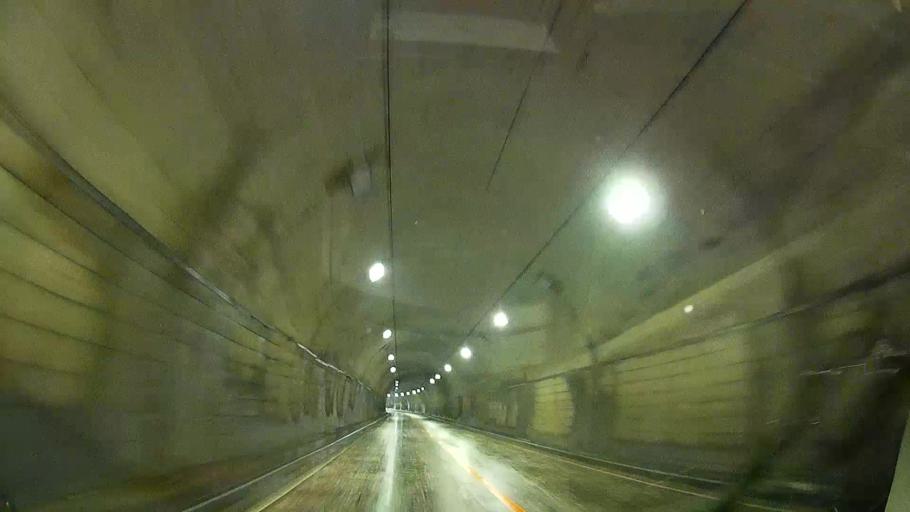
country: JP
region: Kumamoto
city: Aso
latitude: 33.0814
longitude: 131.0625
